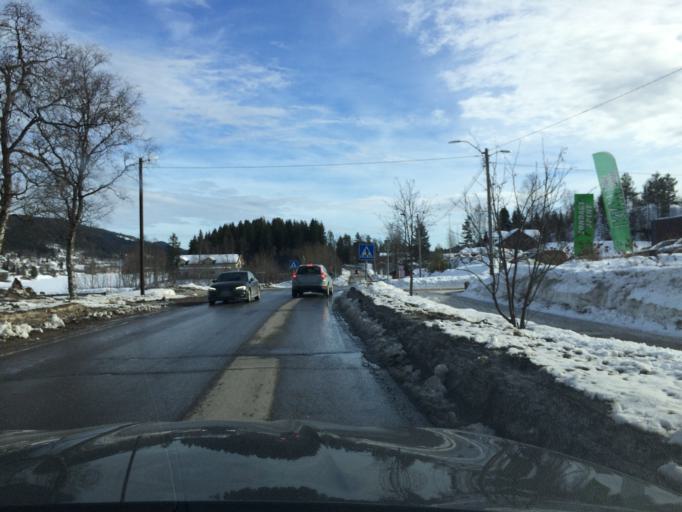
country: NO
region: Hedmark
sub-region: Trysil
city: Innbygda
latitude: 61.3154
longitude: 12.2562
